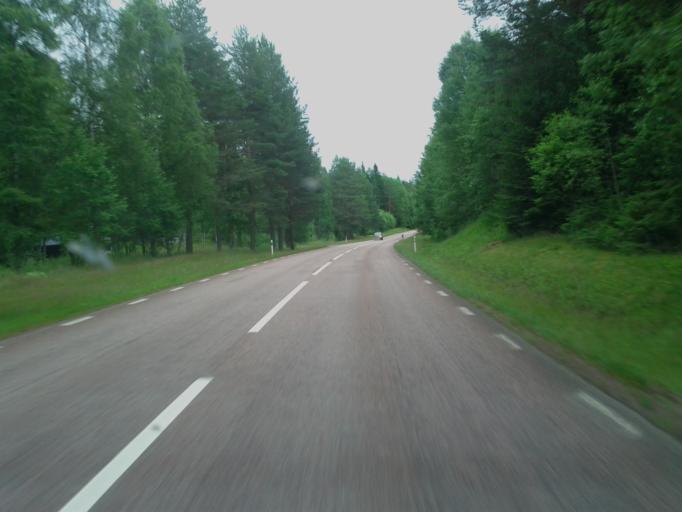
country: SE
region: Dalarna
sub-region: Mora Kommun
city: Mora
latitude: 61.0861
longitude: 14.3205
